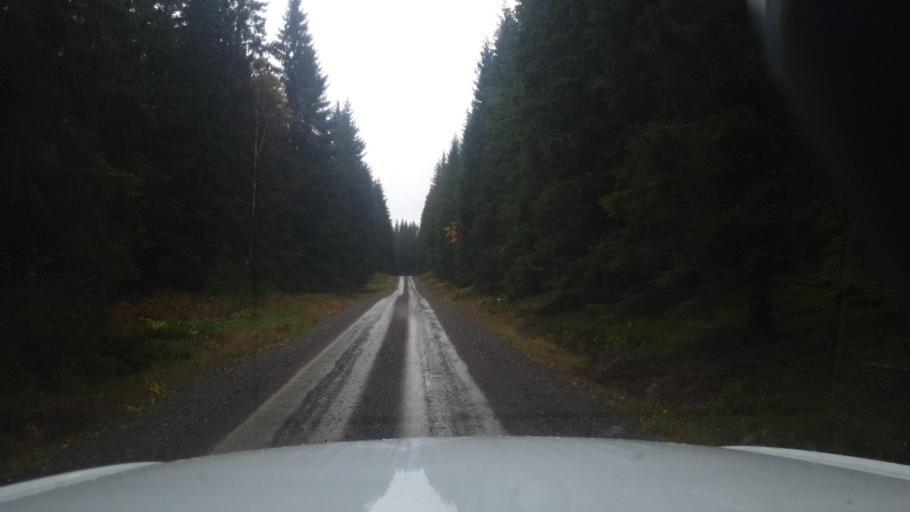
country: SE
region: Vaermland
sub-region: Eda Kommun
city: Charlottenberg
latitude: 60.0363
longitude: 12.6304
